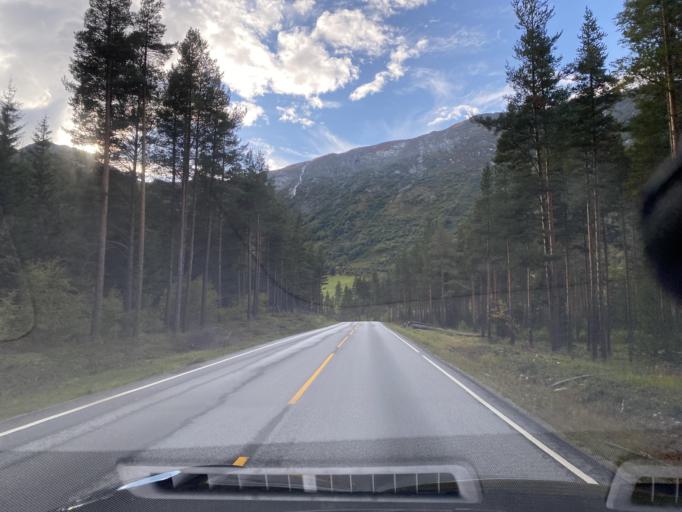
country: NO
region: Oppland
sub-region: Lom
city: Fossbergom
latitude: 61.8089
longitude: 8.4669
